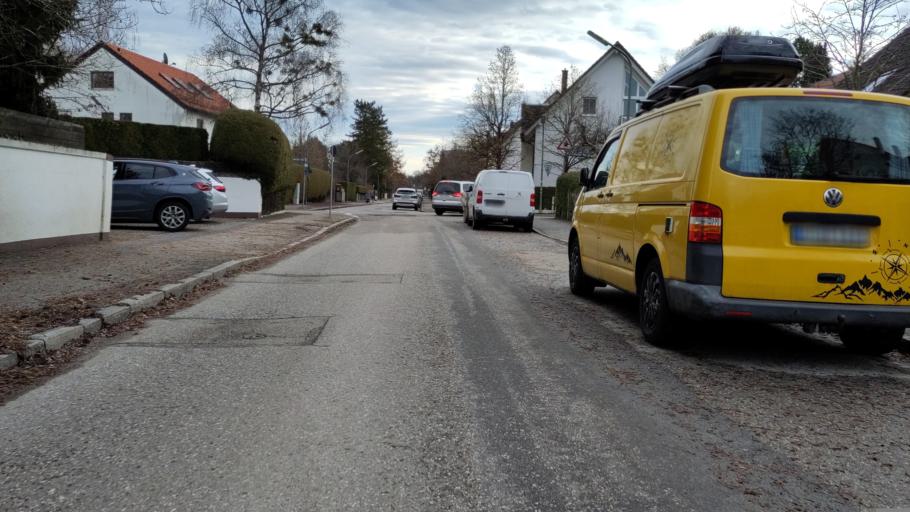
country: DE
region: Bavaria
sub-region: Upper Bavaria
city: Neuried
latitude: 48.0847
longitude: 11.4796
